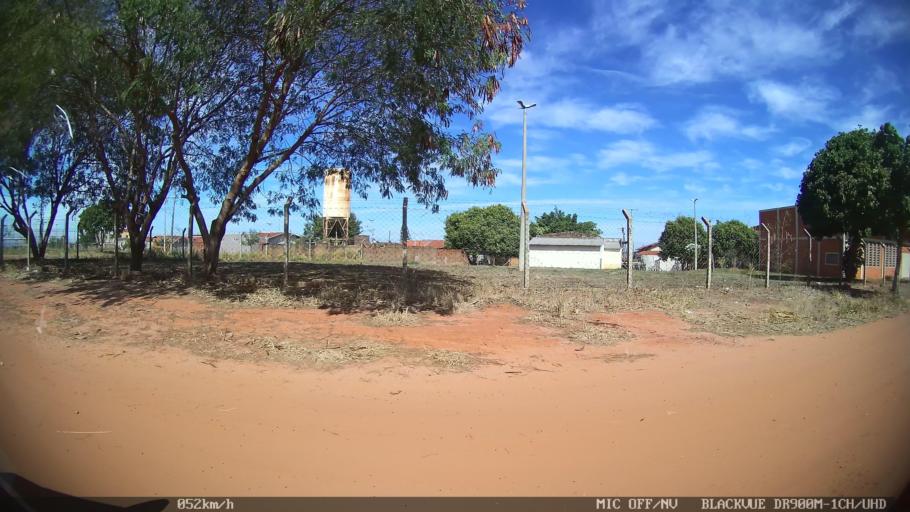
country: BR
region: Sao Paulo
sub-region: Bady Bassitt
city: Bady Bassitt
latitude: -20.8217
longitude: -49.4910
